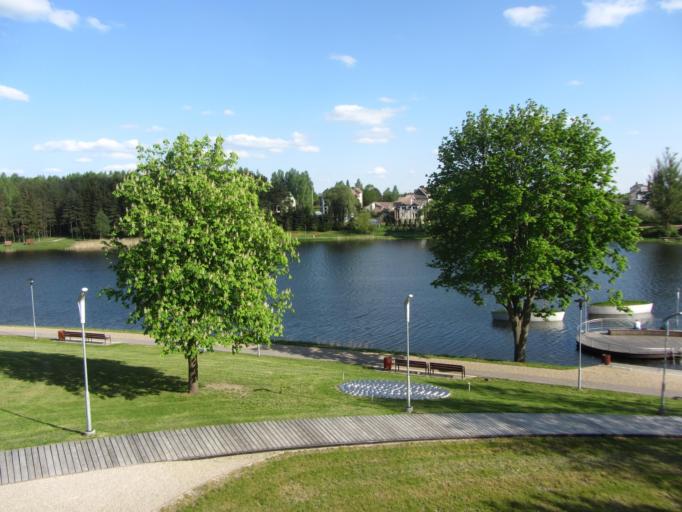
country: LT
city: Moletai
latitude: 55.2318
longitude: 25.4264
